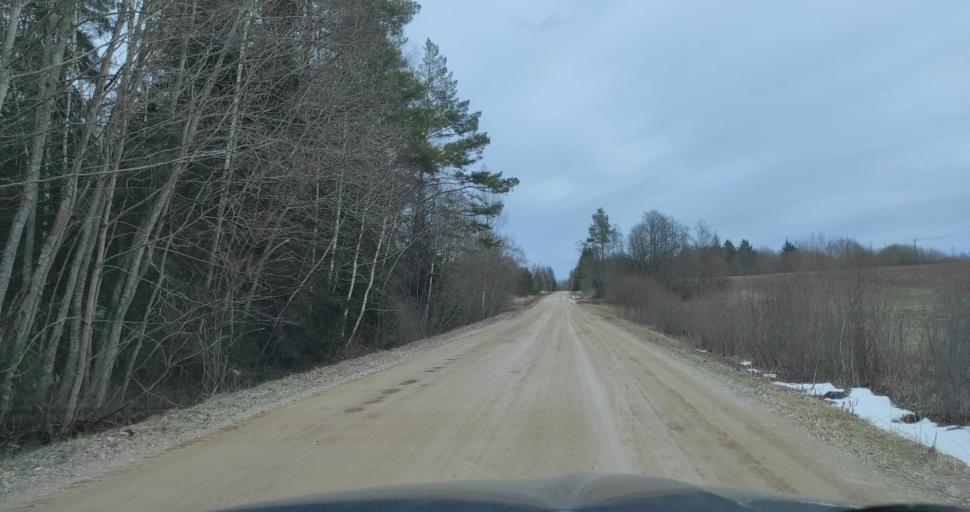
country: LV
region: Tukuma Rajons
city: Tukums
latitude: 57.0821
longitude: 23.0761
